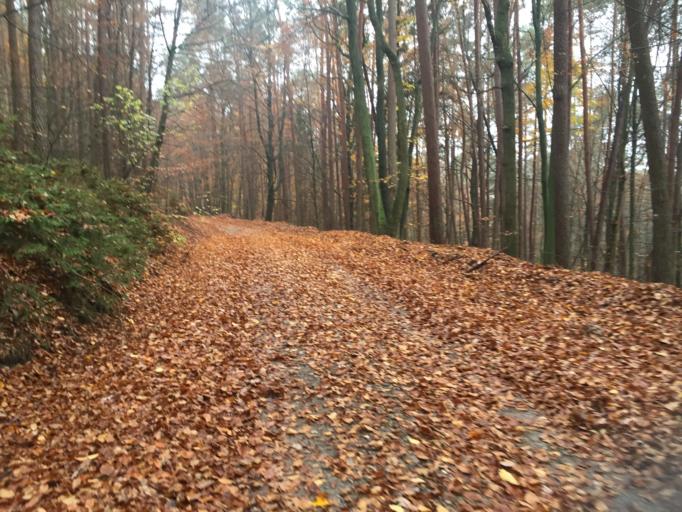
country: DE
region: Baden-Wuerttemberg
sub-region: Karlsruhe Region
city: Heddesbach
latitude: 49.4660
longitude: 8.8475
